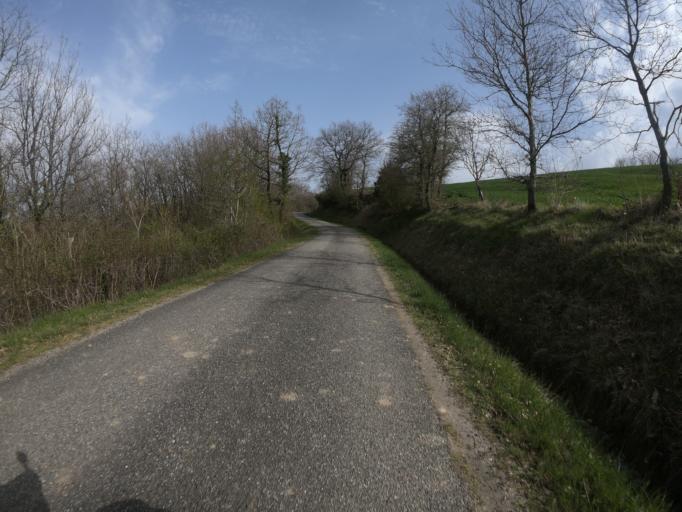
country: FR
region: Languedoc-Roussillon
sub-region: Departement de l'Aude
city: Belpech
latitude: 43.1557
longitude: 1.7760
